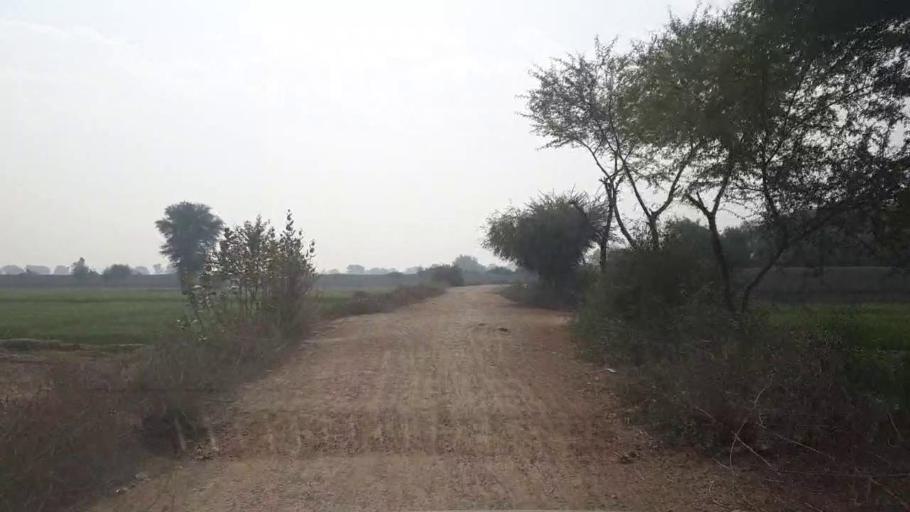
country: PK
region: Sindh
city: Hala
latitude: 25.7948
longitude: 68.4428
